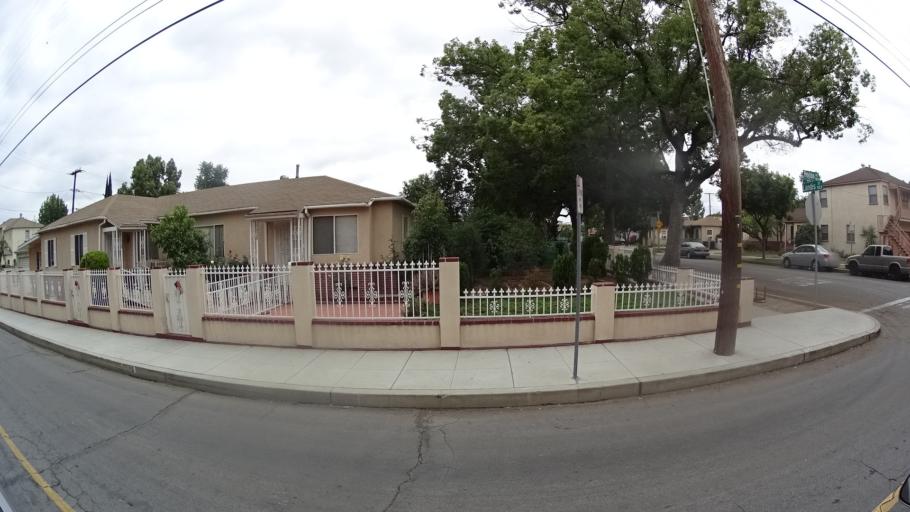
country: US
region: California
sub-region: Los Angeles County
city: Burbank
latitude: 34.1965
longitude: -118.3285
